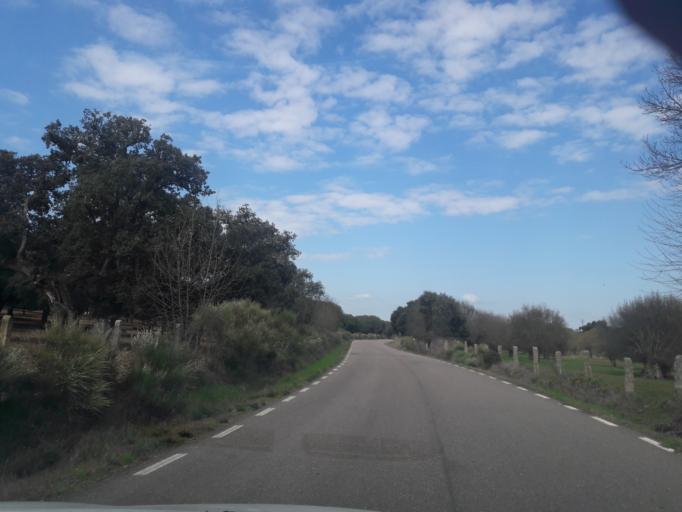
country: ES
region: Castille and Leon
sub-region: Provincia de Salamanca
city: Zamarra
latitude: 40.5549
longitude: -6.4477
